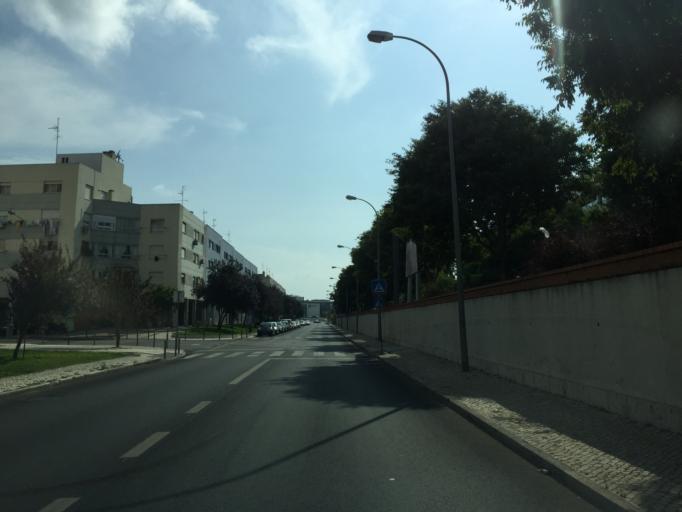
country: PT
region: Lisbon
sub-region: Odivelas
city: Pontinha
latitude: 38.7684
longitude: -9.1803
